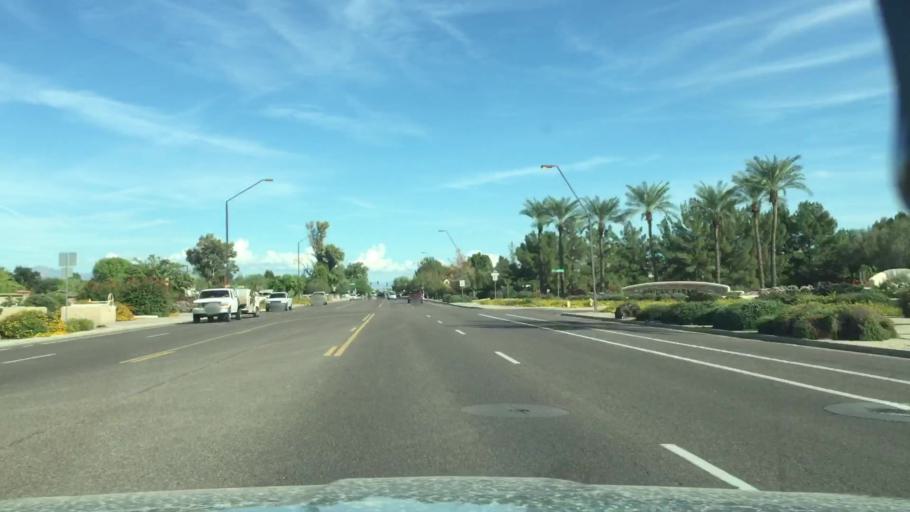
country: US
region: Arizona
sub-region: Maricopa County
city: Gilbert
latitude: 33.3502
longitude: -111.7434
